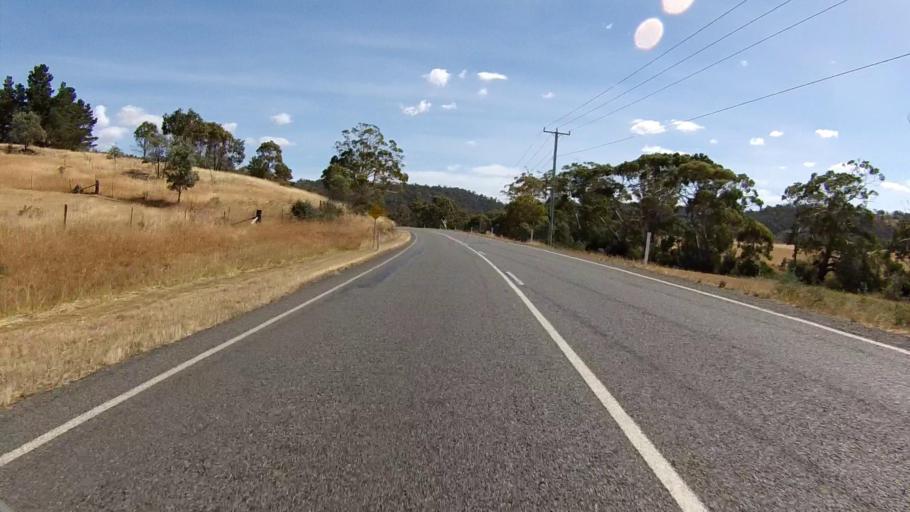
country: AU
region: Tasmania
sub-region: Sorell
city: Sorell
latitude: -42.6068
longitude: 147.7007
